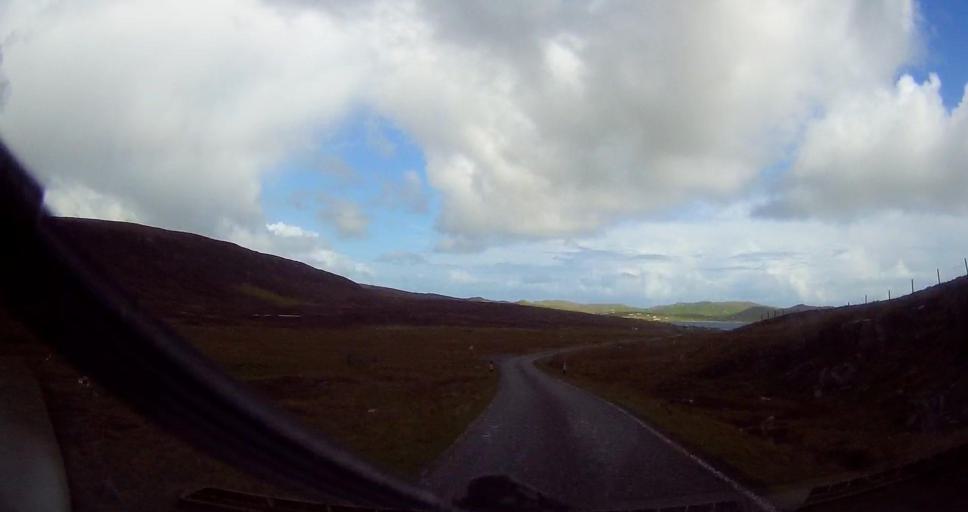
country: GB
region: Scotland
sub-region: Shetland Islands
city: Lerwick
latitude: 60.5638
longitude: -1.3345
